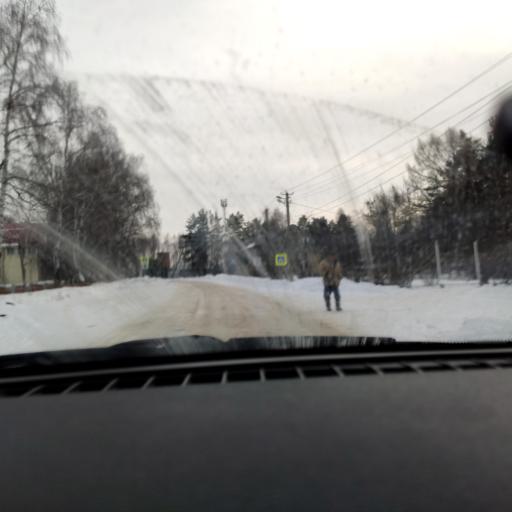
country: RU
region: Bashkortostan
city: Iglino
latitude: 54.7689
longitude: 56.5336
